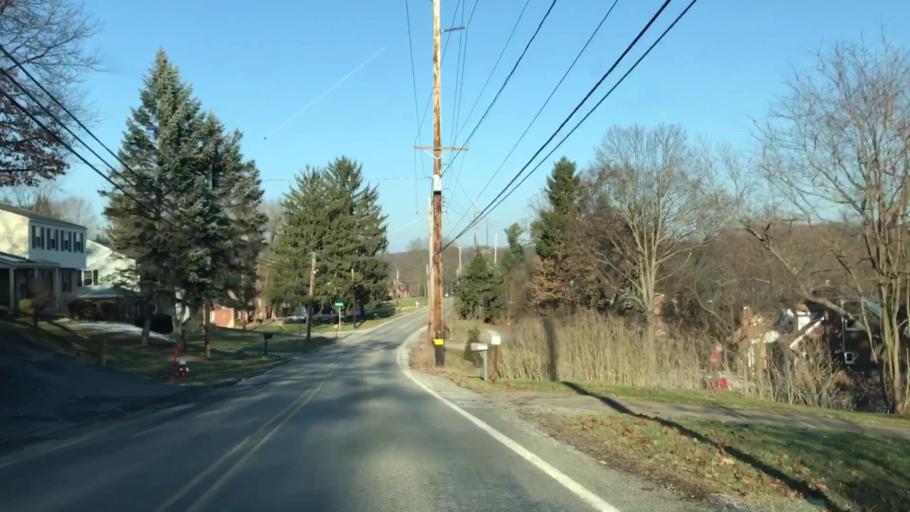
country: US
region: Pennsylvania
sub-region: Allegheny County
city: Allison Park
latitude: 40.5770
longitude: -79.9978
